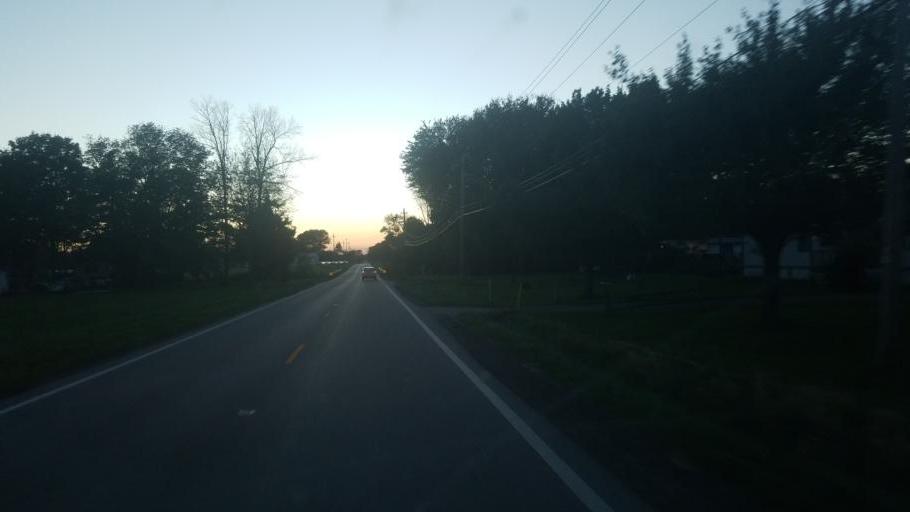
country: US
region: Ohio
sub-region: Ashtabula County
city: Andover
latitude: 41.7515
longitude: -80.5878
